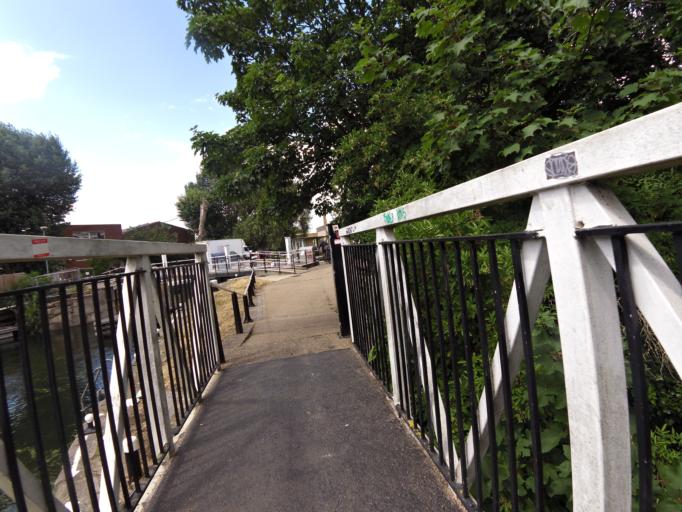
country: GB
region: England
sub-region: Greater London
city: Poplar
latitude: 51.5377
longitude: -0.0207
